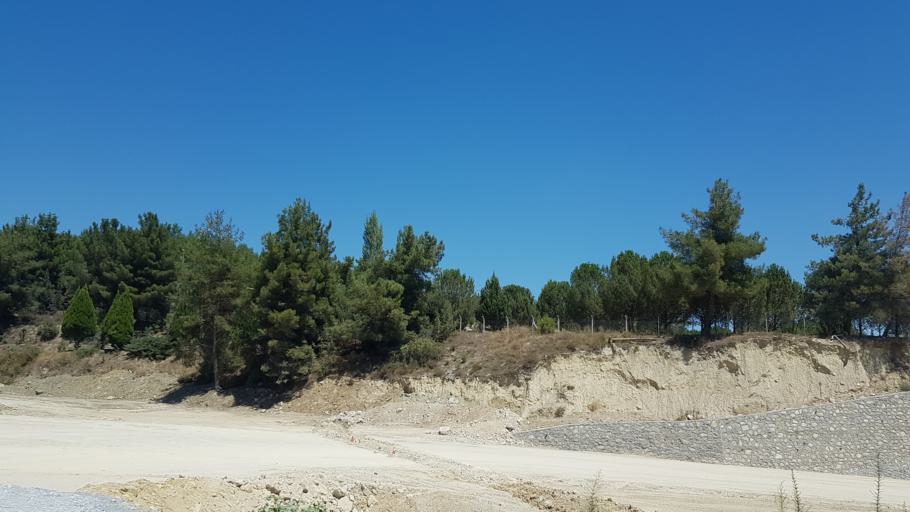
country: TR
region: Mugla
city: Yatagan
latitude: 37.3183
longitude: 28.0824
